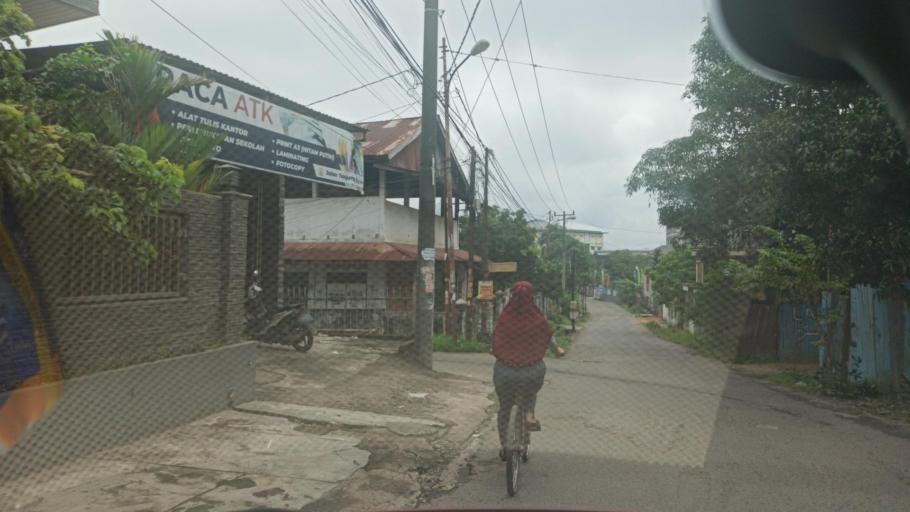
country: ID
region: South Sumatra
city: Palembang
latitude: -2.9327
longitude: 104.7754
